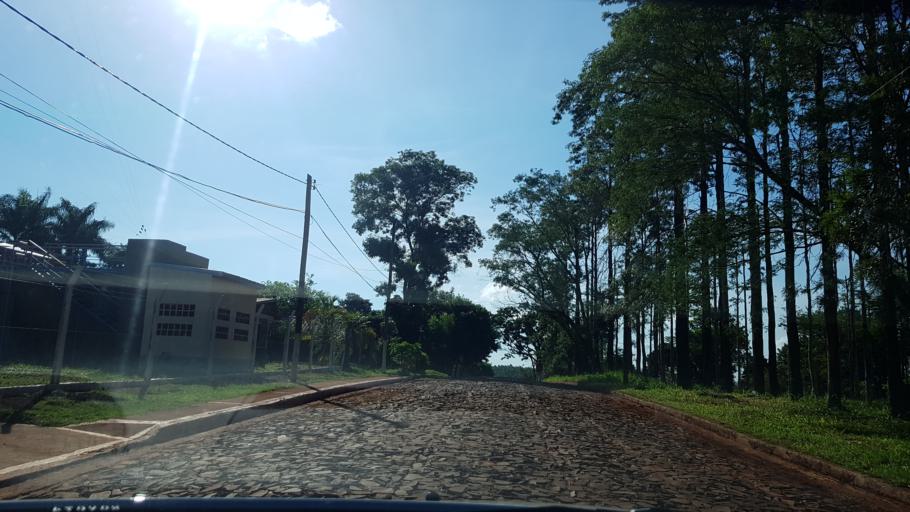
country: AR
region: Misiones
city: Puerto Libertad
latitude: -25.9166
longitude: -54.5770
